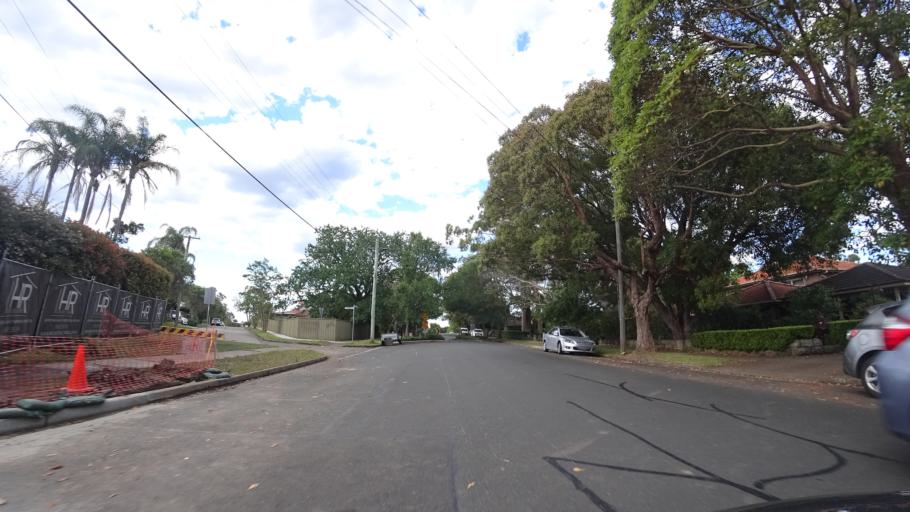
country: AU
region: New South Wales
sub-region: Willoughby
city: Chatswood
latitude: -33.7976
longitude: 151.1924
